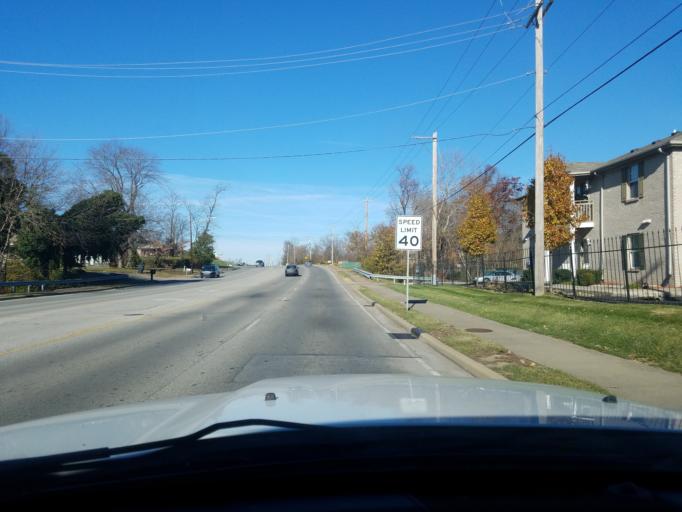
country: US
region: Indiana
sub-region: Floyd County
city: New Albany
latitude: 38.3281
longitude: -85.8000
